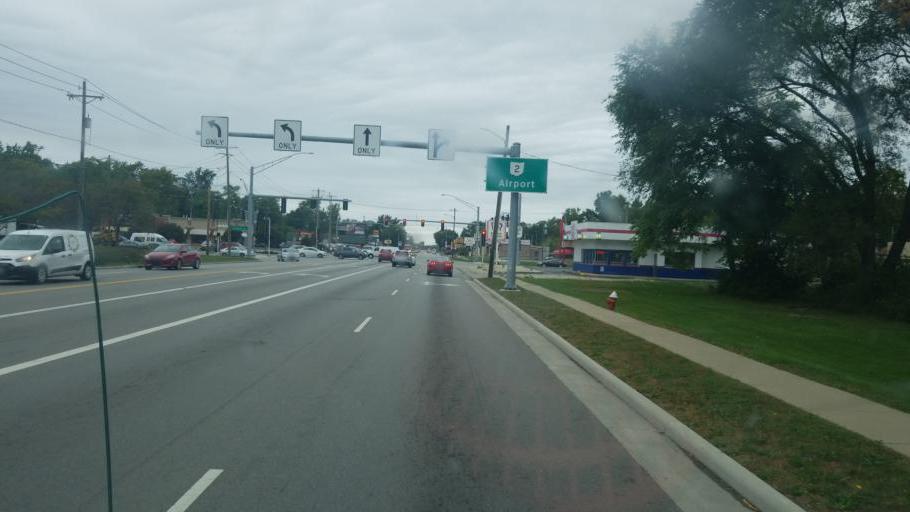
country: US
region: Ohio
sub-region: Lucas County
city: Holland
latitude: 41.6156
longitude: -83.6645
